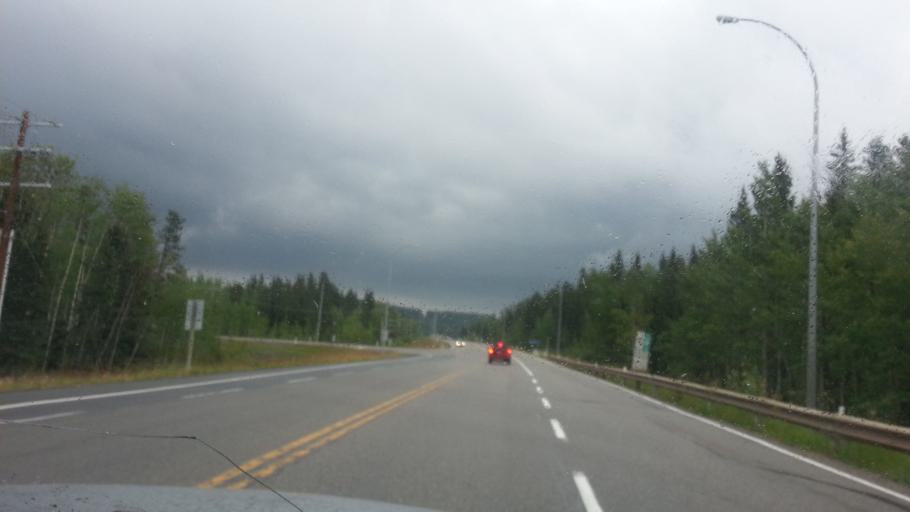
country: CA
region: Alberta
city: Cochrane
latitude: 50.9215
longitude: -114.5620
